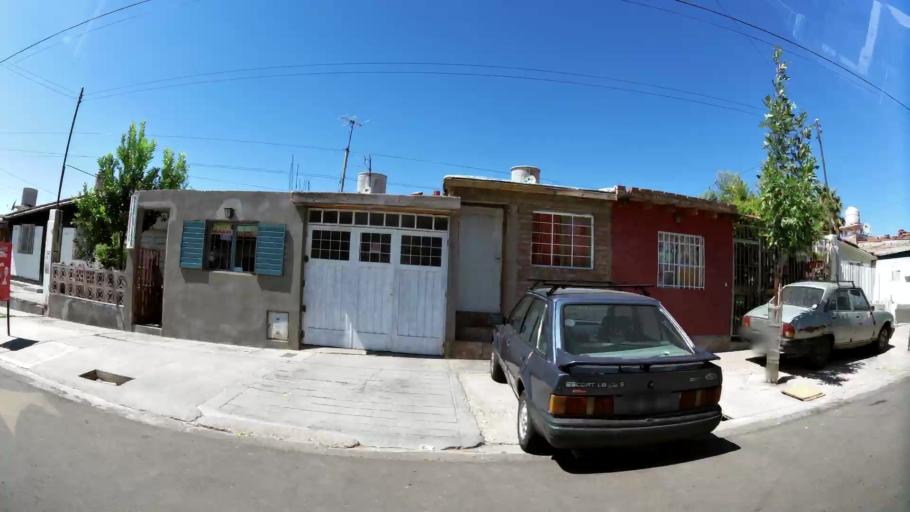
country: AR
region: Mendoza
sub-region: Departamento de Godoy Cruz
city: Godoy Cruz
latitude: -32.9464
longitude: -68.8686
